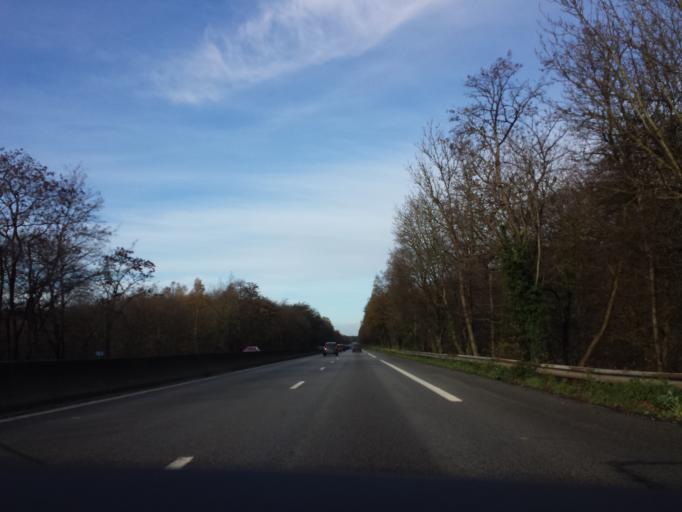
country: FR
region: Ile-de-France
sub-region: Departement des Yvelines
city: Noisy-le-Roi
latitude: 48.8530
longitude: 2.0631
